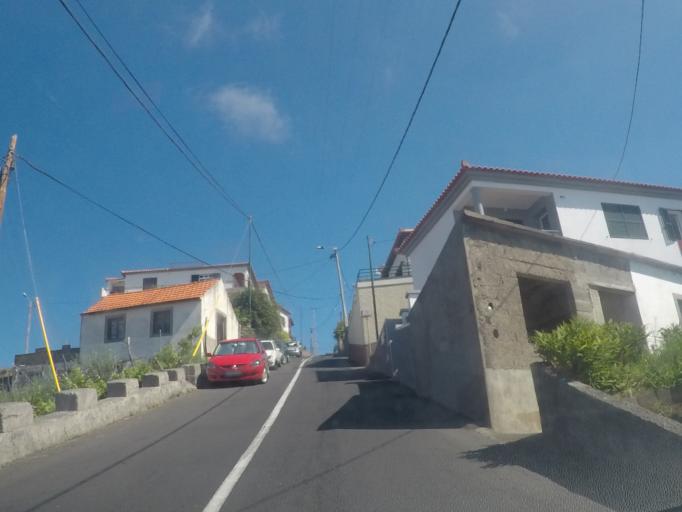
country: PT
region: Madeira
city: Camara de Lobos
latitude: 32.6741
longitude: -16.9645
